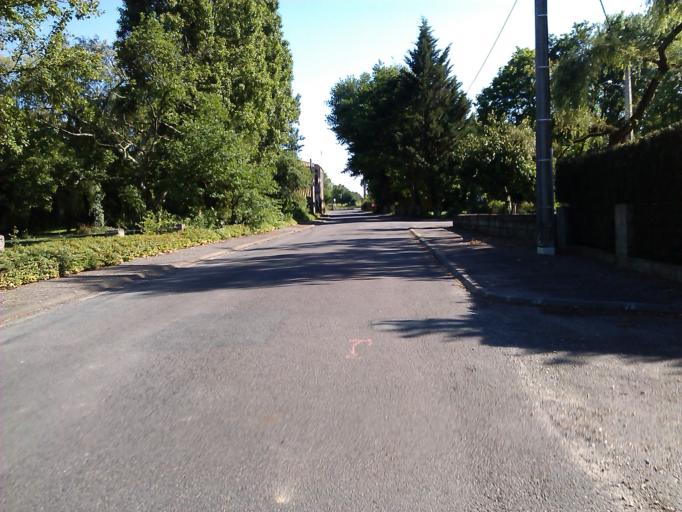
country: FR
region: Aquitaine
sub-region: Departement de la Gironde
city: Cezac
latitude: 45.0761
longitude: -0.4053
